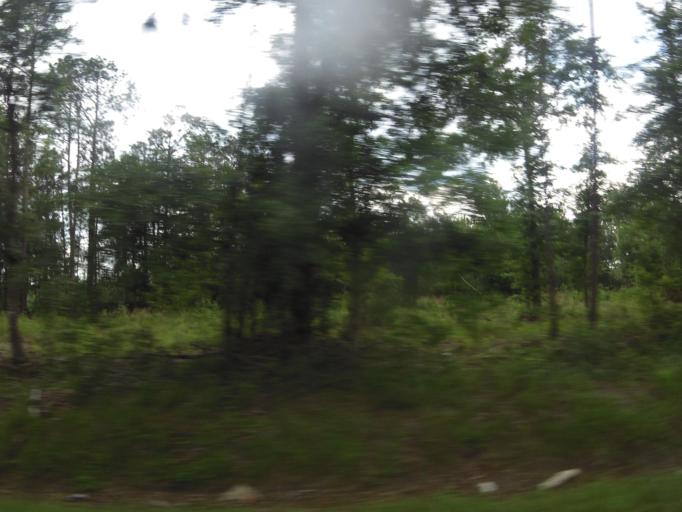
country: US
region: Florida
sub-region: Duval County
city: Baldwin
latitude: 30.3282
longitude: -81.8734
